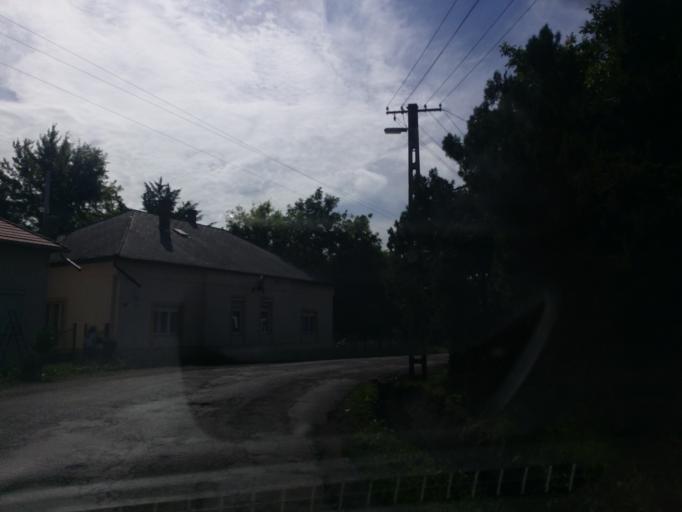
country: HU
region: Heves
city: Heves
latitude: 47.6168
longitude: 20.3585
